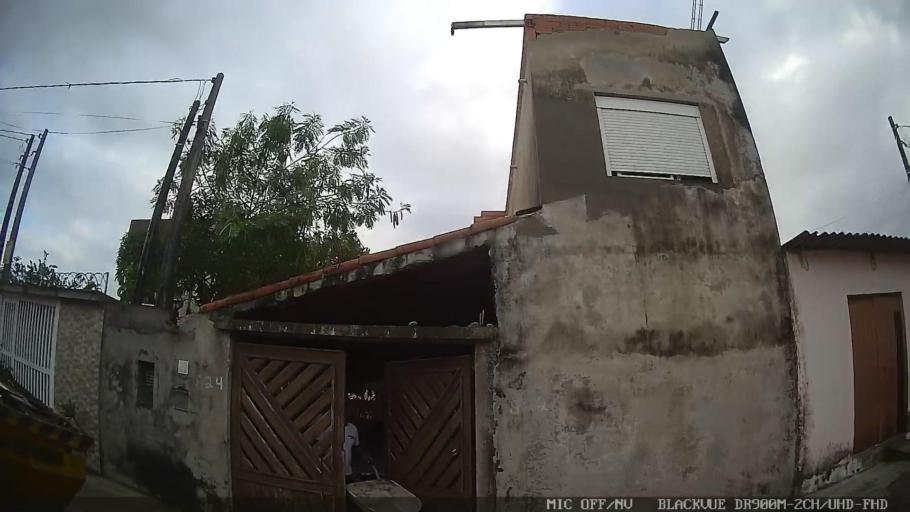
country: BR
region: Sao Paulo
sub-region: Itanhaem
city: Itanhaem
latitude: -24.1953
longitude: -46.8202
